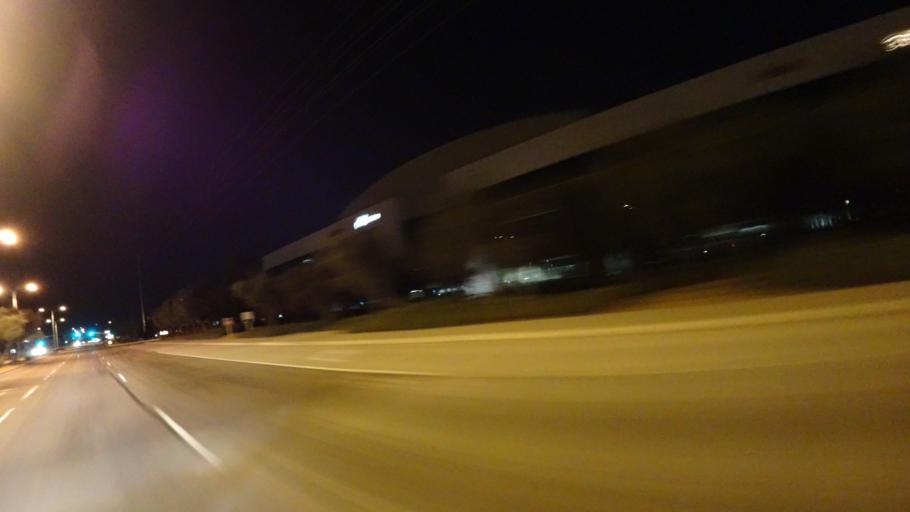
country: US
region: Arizona
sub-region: Maricopa County
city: San Carlos
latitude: 33.3204
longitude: -111.8954
